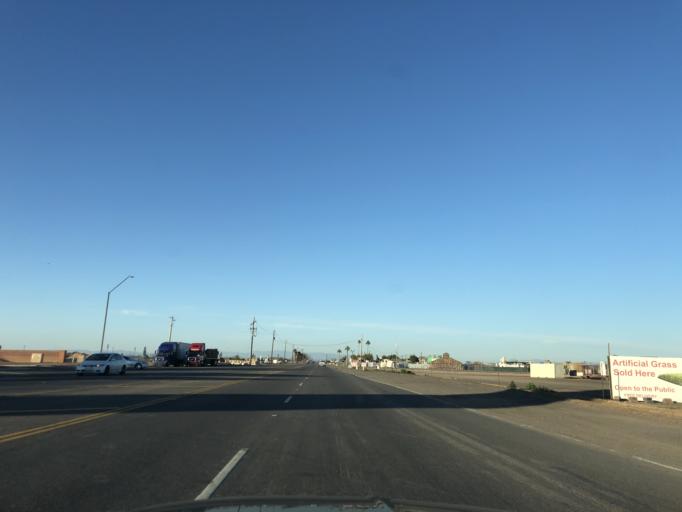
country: US
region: Arizona
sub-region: Maricopa County
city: Tolleson
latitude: 33.4672
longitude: -112.2725
